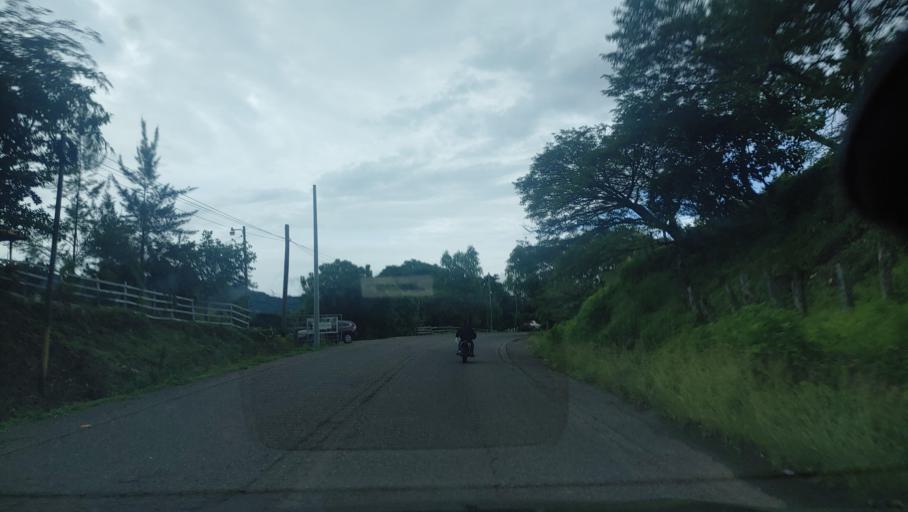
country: HN
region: Choluteca
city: Corpus
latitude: 13.3658
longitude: -86.9944
